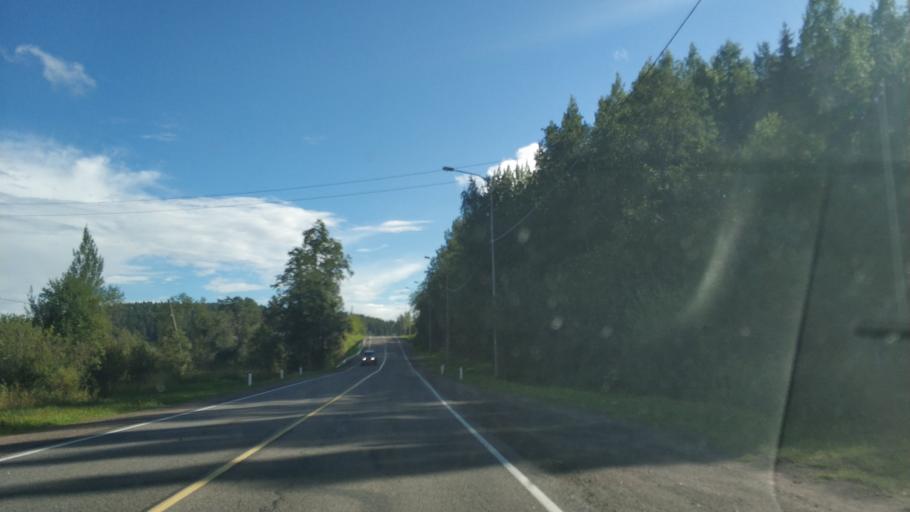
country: RU
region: Republic of Karelia
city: Sortavala
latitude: 61.6658
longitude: 30.6541
